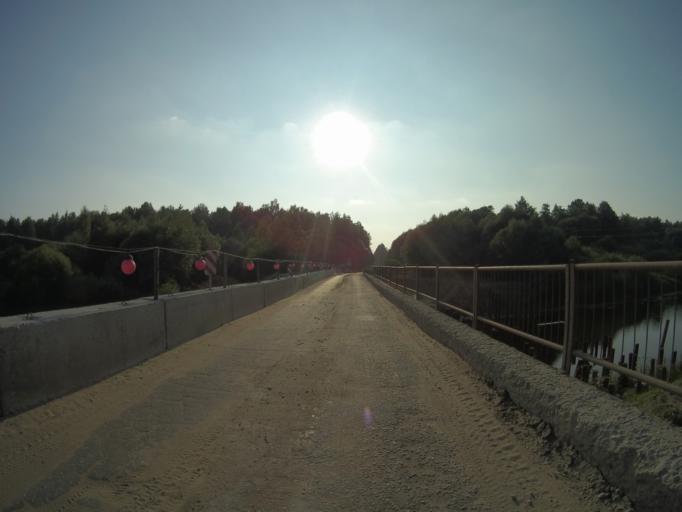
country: RU
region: Vladimir
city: Sudogda
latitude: 56.0743
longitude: 40.7800
